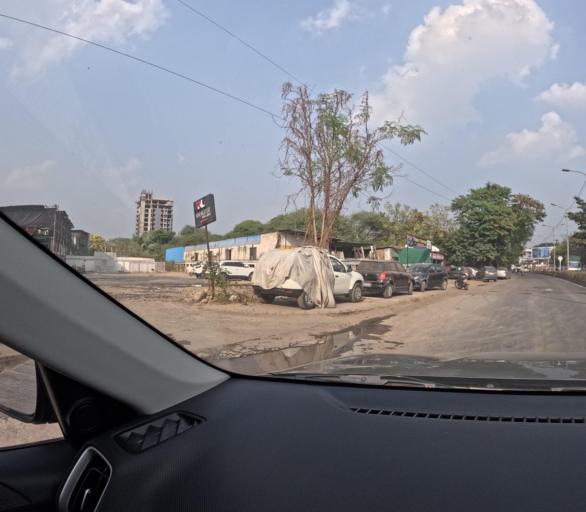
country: IN
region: Maharashtra
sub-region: Pune Division
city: Pune
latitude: 18.5319
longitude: 73.9159
